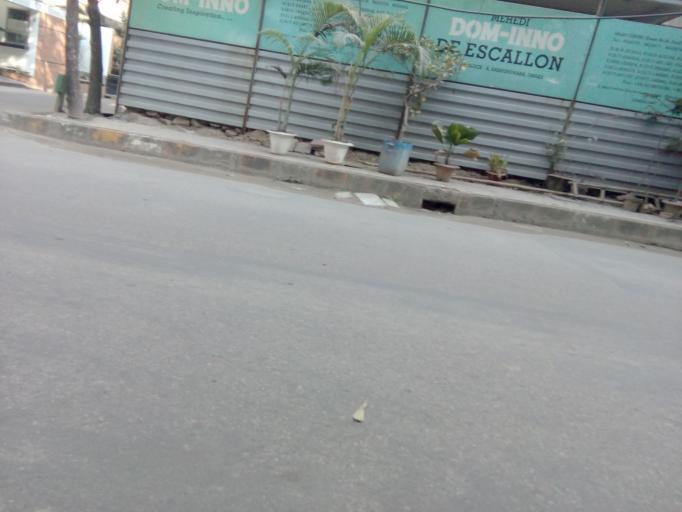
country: BD
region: Dhaka
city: Paltan
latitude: 23.8118
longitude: 90.4282
